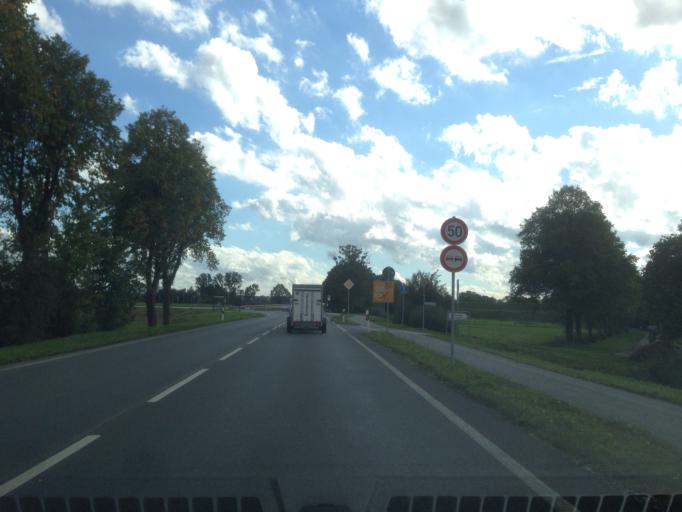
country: DE
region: North Rhine-Westphalia
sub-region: Regierungsbezirk Munster
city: Muenster
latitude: 51.8920
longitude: 7.5776
